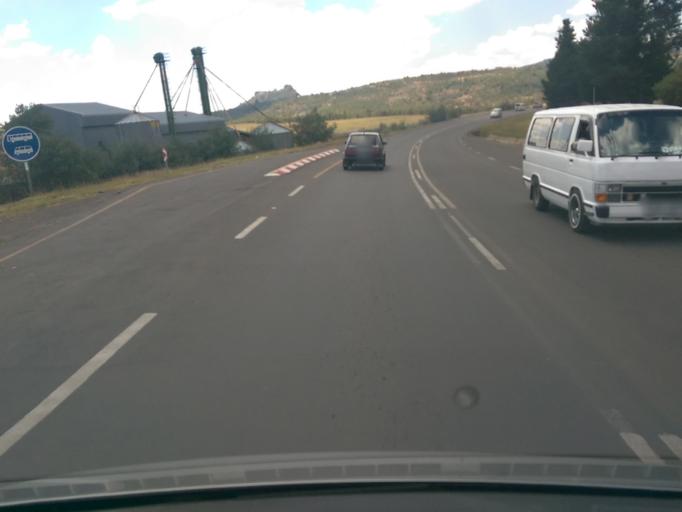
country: LS
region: Maseru
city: Maseru
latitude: -29.3949
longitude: 27.5511
